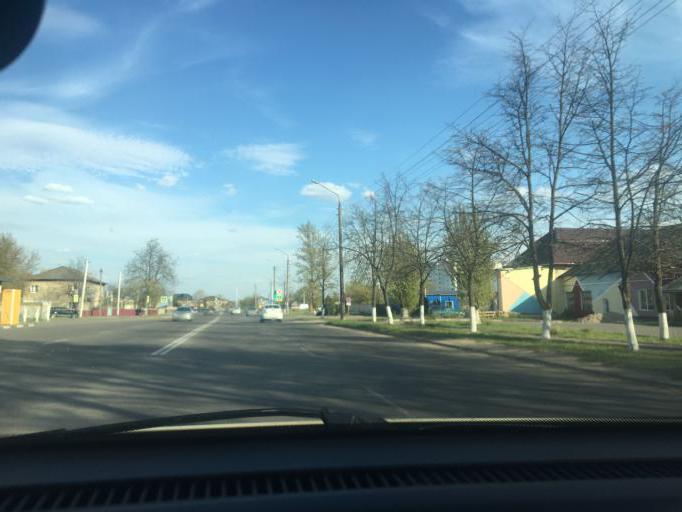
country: BY
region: Mogilev
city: Babruysk
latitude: 53.1490
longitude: 29.1908
